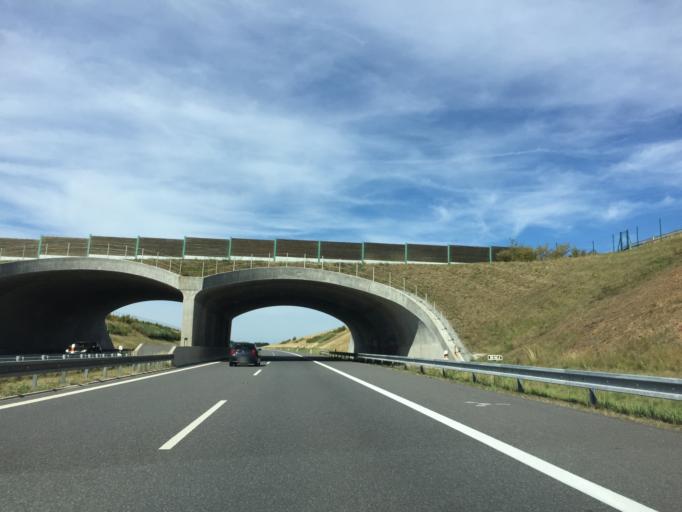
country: CZ
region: Jihocesky
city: Sobeslav
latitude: 49.3065
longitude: 14.7386
